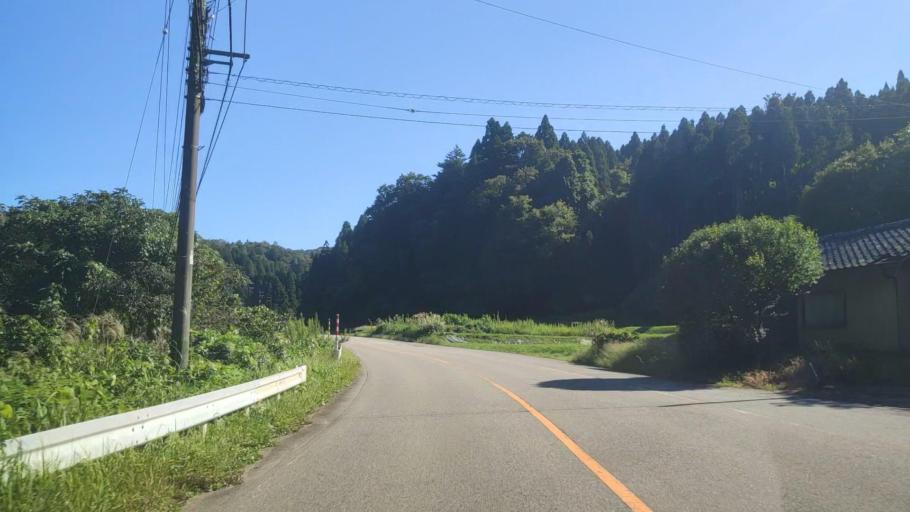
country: JP
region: Ishikawa
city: Nanao
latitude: 37.3332
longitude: 137.2074
